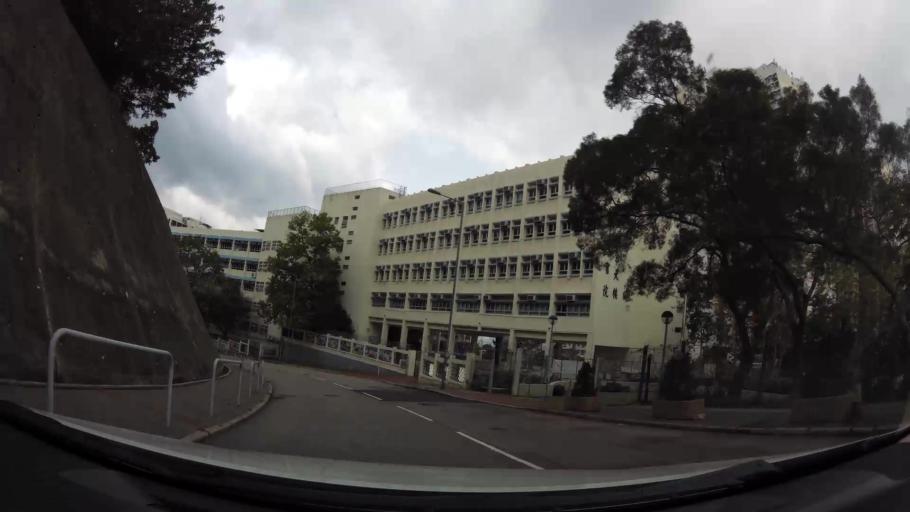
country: HK
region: Kowloon City
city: Kowloon
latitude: 22.3194
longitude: 114.2188
